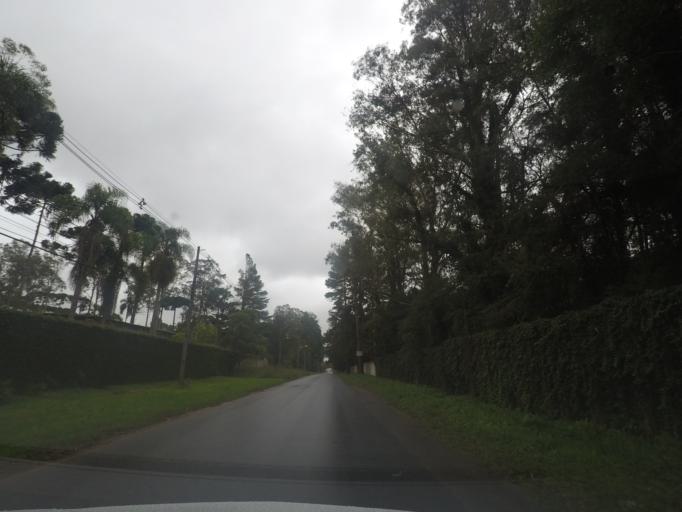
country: BR
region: Parana
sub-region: Pinhais
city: Pinhais
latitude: -25.3899
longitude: -49.1508
